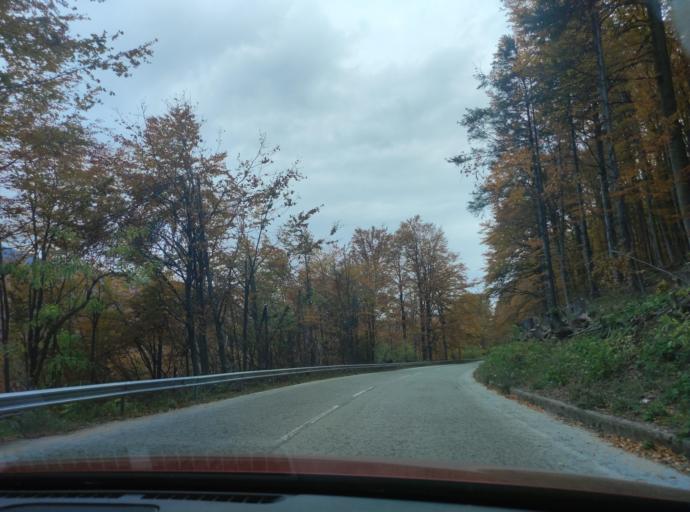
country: BG
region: Montana
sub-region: Obshtina Berkovitsa
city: Berkovitsa
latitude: 43.1406
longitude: 23.1423
